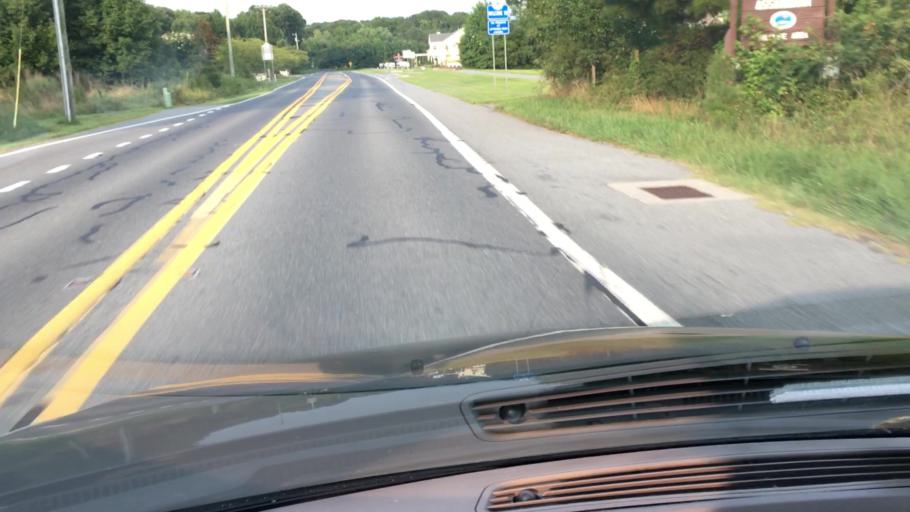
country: US
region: Delaware
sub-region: Sussex County
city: Ocean View
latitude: 38.5190
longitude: -75.0762
